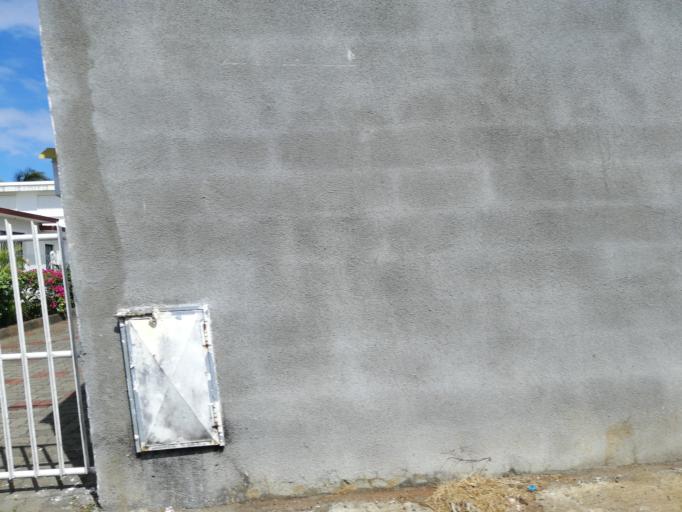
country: MU
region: Moka
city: Moka
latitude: -20.2193
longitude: 57.4759
